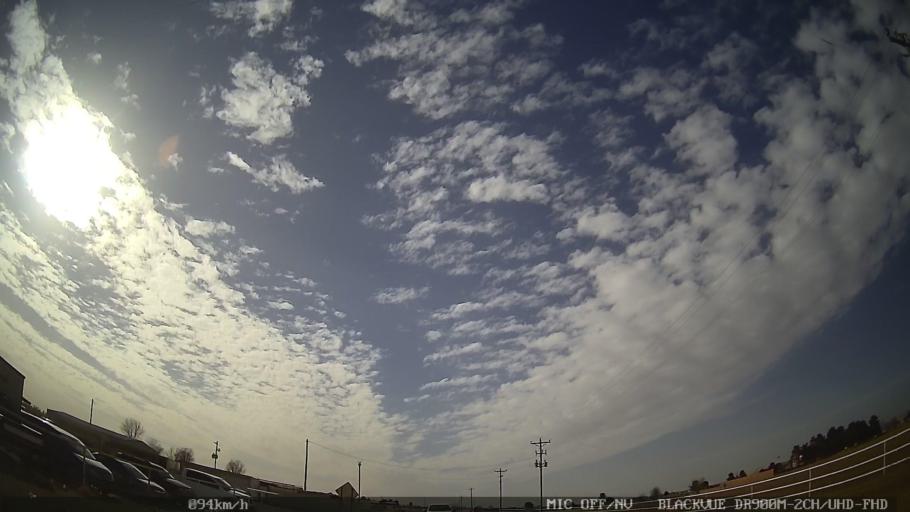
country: US
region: New Mexico
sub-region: Curry County
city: Clovis
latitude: 34.4194
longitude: -103.1452
